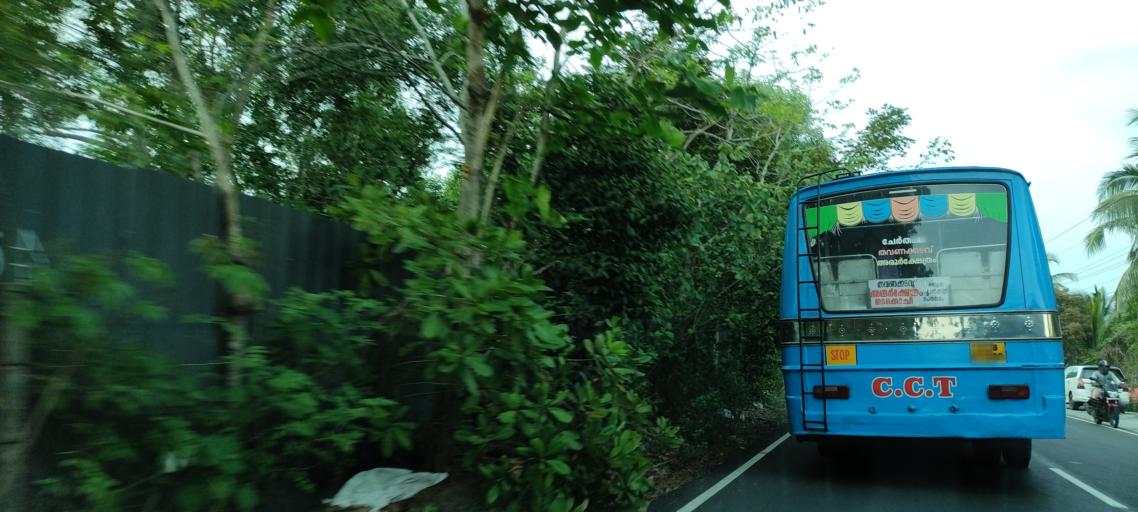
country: IN
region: Kerala
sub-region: Alappuzha
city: Kutiatodu
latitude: 9.7839
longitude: 76.3599
